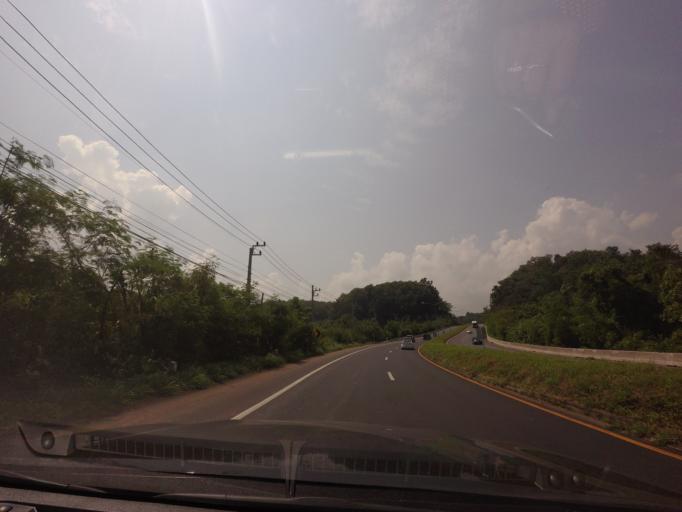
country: TH
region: Phrae
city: Den Chai
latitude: 17.8869
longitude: 100.0491
